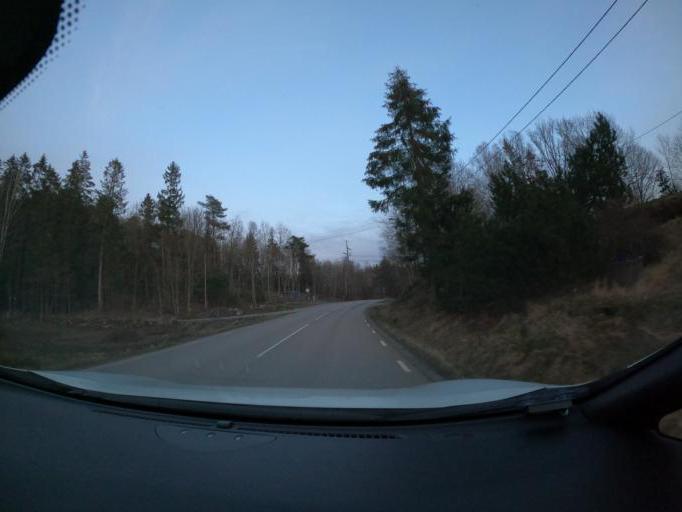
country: SE
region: Vaestra Goetaland
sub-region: Harryda Kommun
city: Landvetter
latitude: 57.6406
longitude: 12.1769
